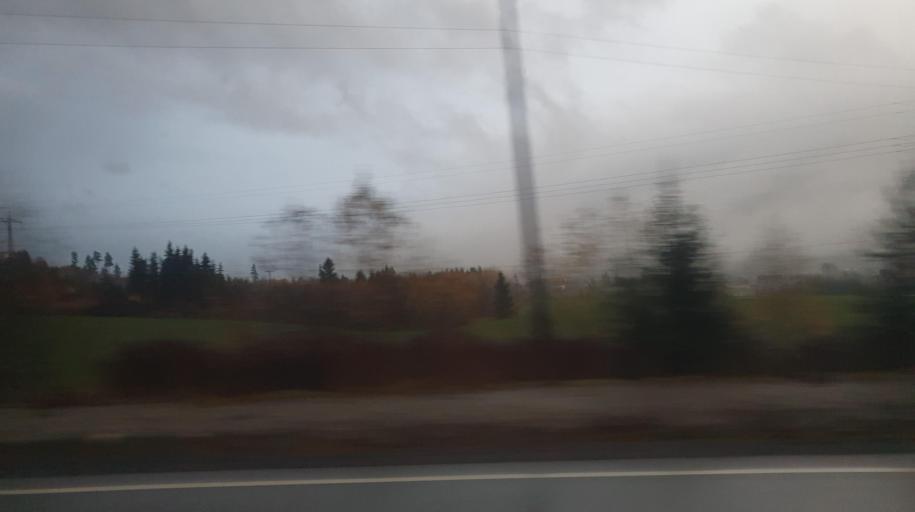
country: NO
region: Buskerud
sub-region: Modum
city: Vikersund
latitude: 59.9809
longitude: 9.9897
